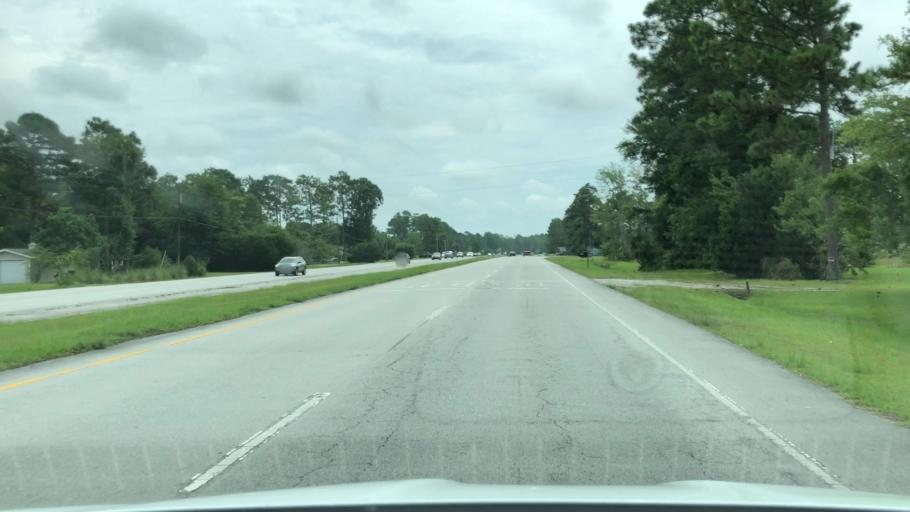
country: US
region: North Carolina
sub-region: Carteret County
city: Newport
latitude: 34.8312
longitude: -76.8792
